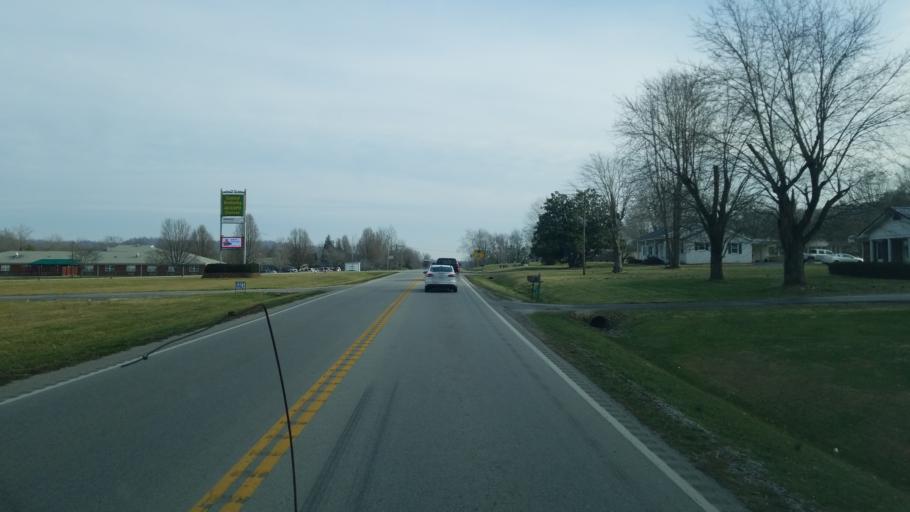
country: US
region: Kentucky
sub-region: Casey County
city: Liberty
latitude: 37.3086
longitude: -84.9435
